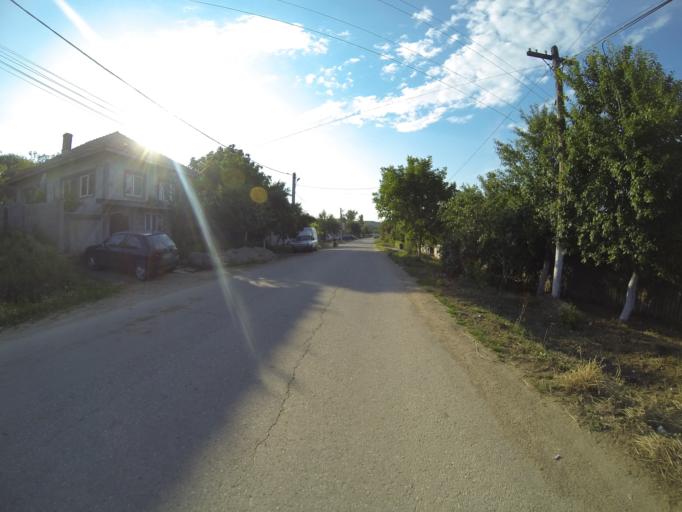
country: RO
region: Dolj
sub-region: Comuna Tuglui
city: Tuglui
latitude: 44.1953
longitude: 23.8055
